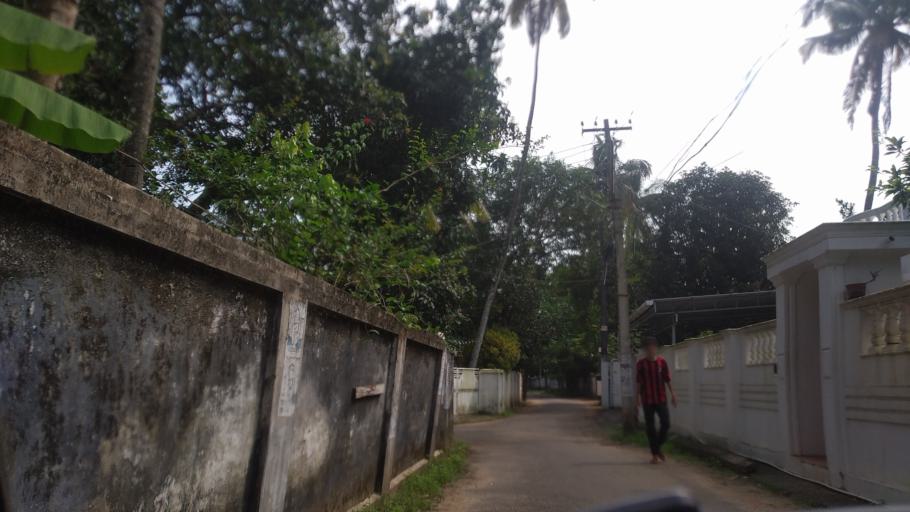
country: IN
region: Kerala
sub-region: Ernakulam
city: Elur
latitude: 10.0856
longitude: 76.2108
